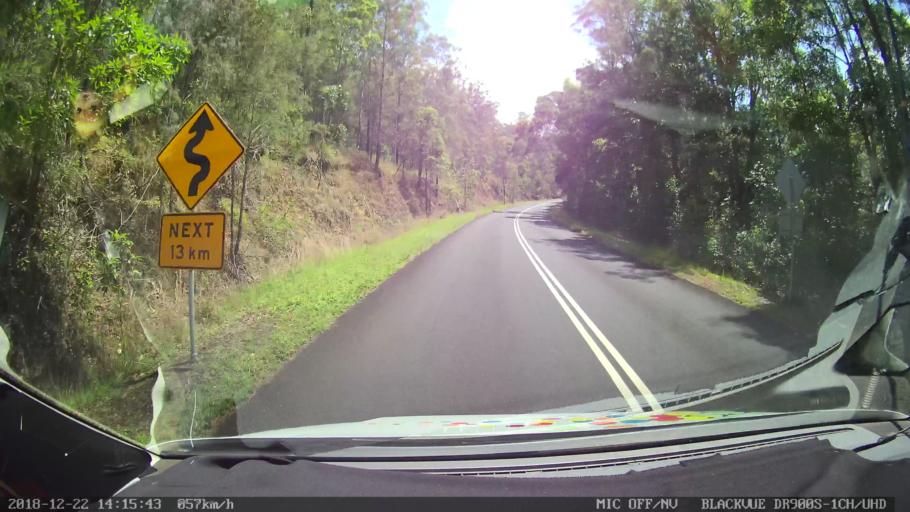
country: AU
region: New South Wales
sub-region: Clarence Valley
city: Coutts Crossing
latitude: -30.0028
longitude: 152.6757
